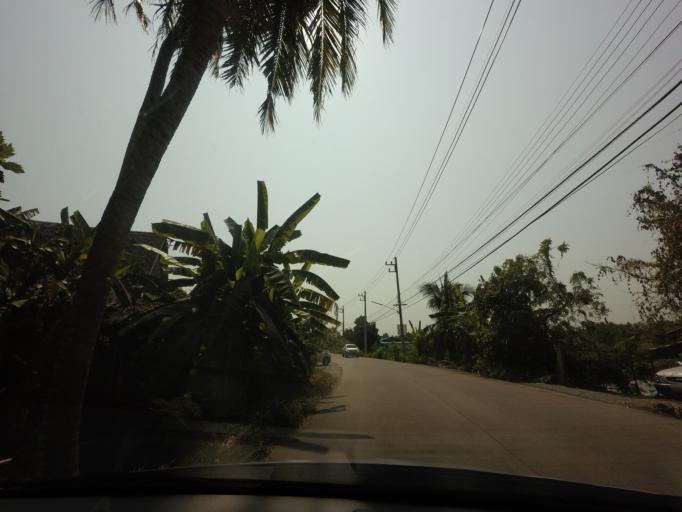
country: TH
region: Nakhon Pathom
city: Sam Phran
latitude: 13.7524
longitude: 100.2613
